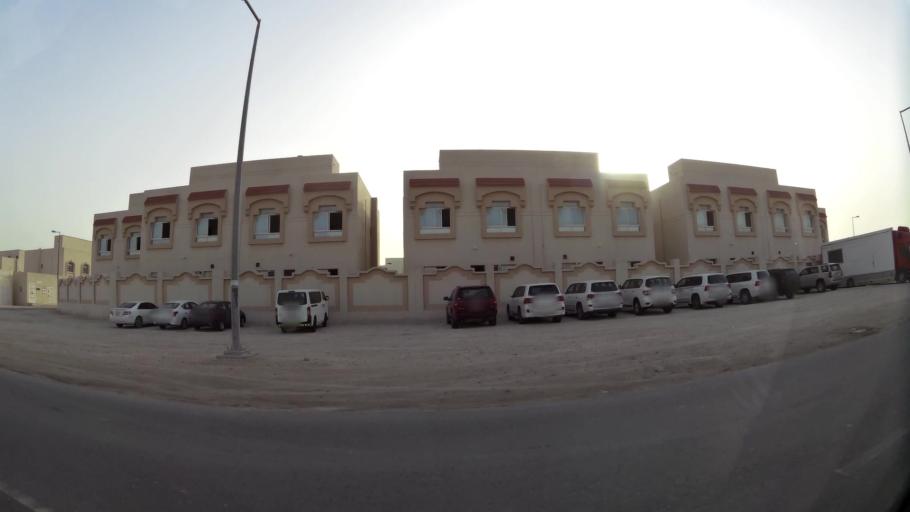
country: QA
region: Baladiyat ar Rayyan
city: Ar Rayyan
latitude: 25.2395
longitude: 51.4500
